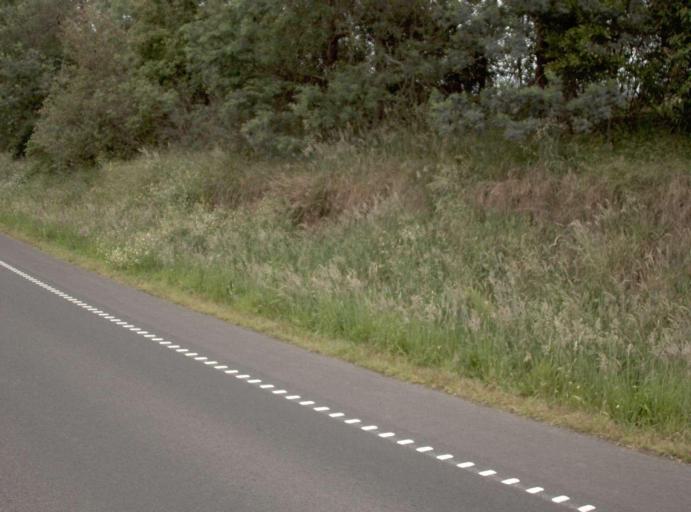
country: AU
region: Victoria
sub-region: Bass Coast
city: North Wonthaggi
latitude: -38.4431
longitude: 145.8302
